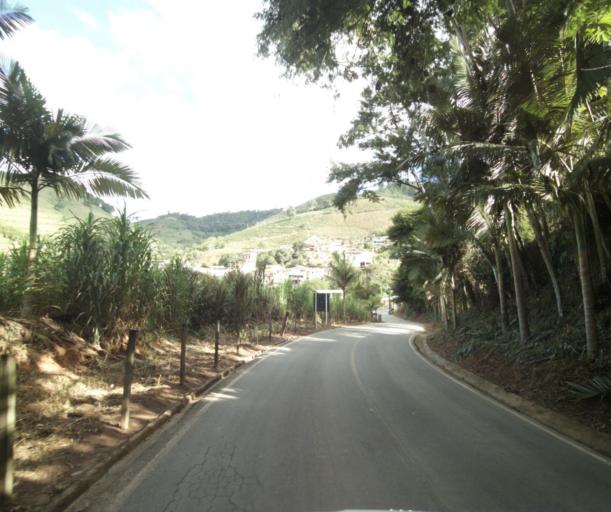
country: BR
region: Espirito Santo
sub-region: Irupi
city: Irupi
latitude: -20.5383
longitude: -41.6683
